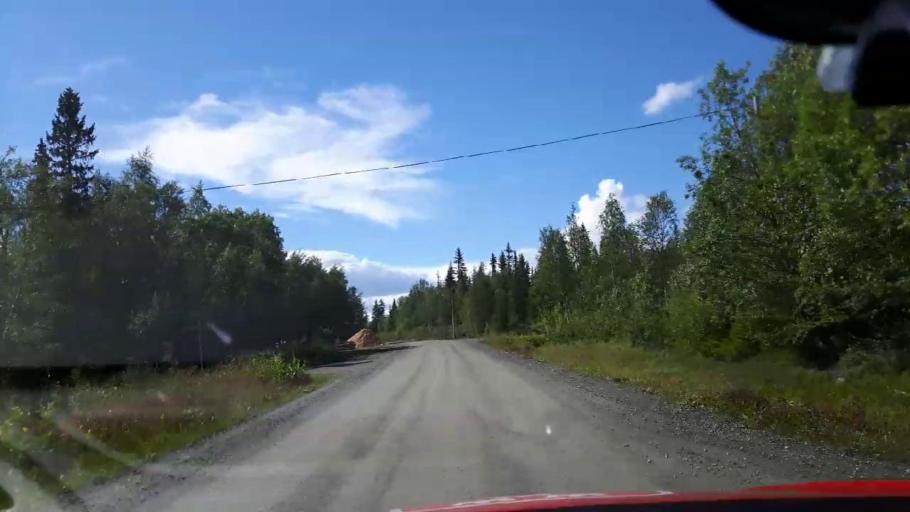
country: SE
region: Jaemtland
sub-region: Are Kommun
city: Are
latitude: 63.2182
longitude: 13.0696
